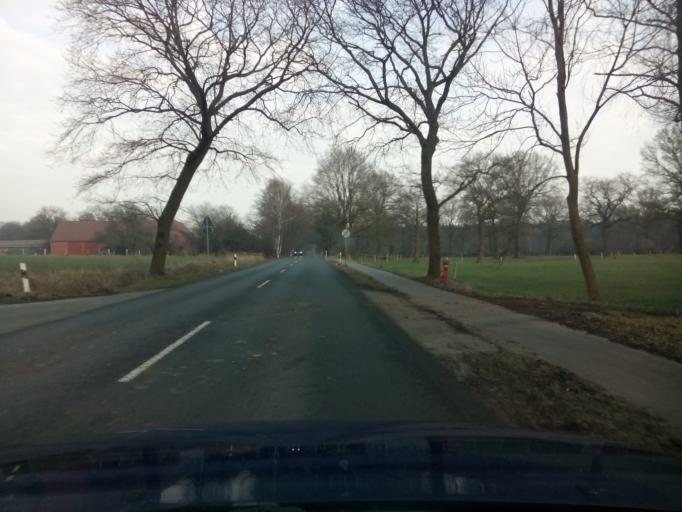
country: DE
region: Lower Saxony
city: Ritterhude
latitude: 53.2305
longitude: 8.7271
